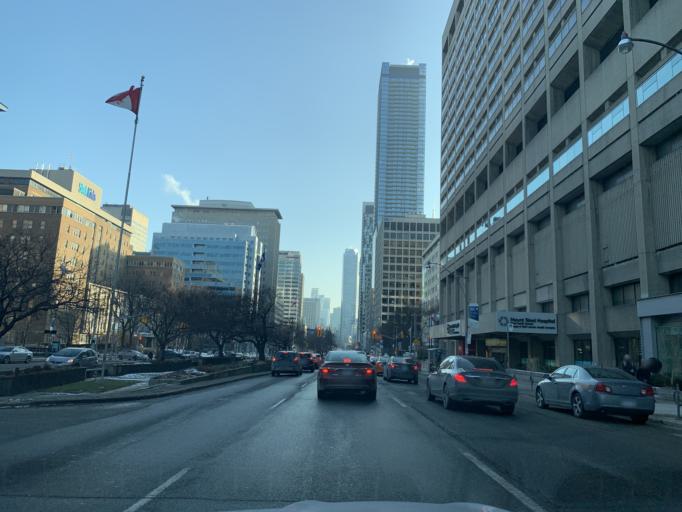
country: CA
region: Ontario
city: Toronto
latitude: 43.6583
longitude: -79.3900
